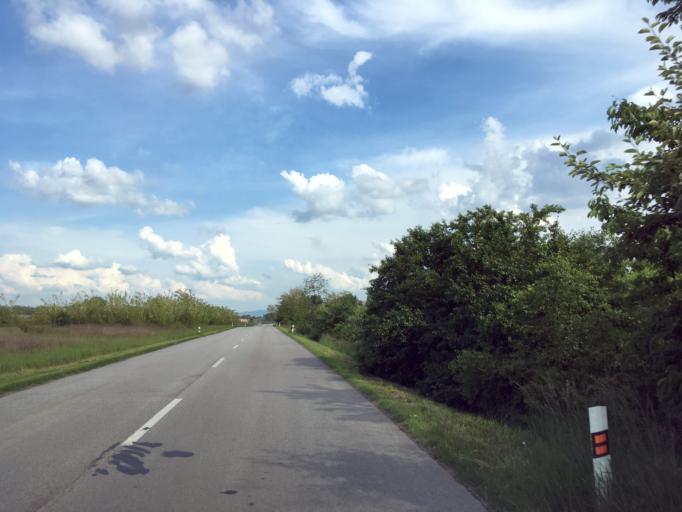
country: HU
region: Komarom-Esztergom
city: Almasfuzito
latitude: 47.7996
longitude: 18.2412
